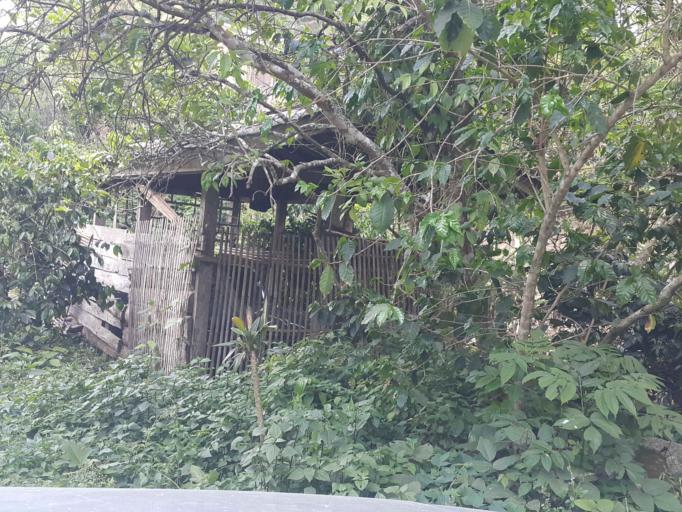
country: TH
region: Chiang Mai
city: Mae On
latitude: 18.9202
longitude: 99.3589
